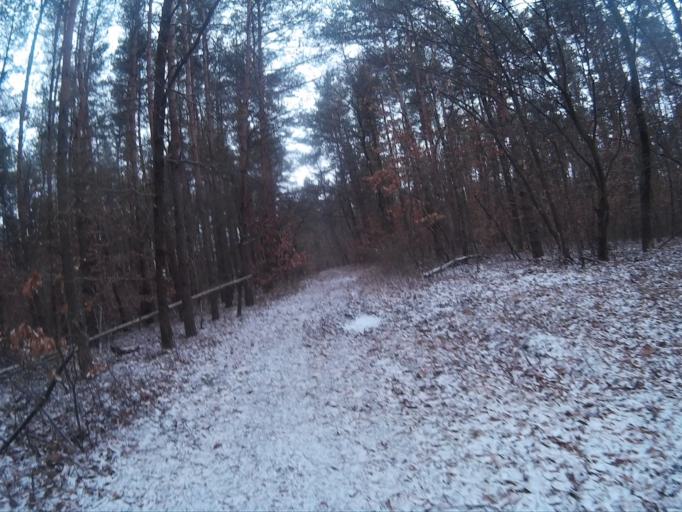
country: HU
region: Borsod-Abauj-Zemplen
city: Halmaj
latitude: 48.3845
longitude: 20.9017
